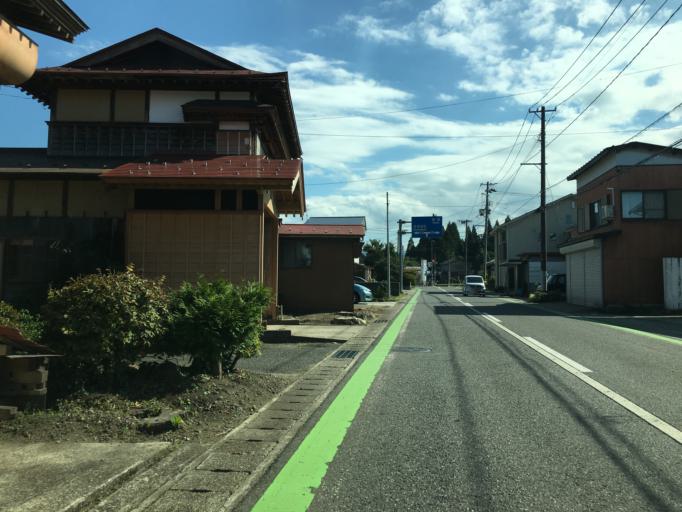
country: JP
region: Niigata
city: Suibara
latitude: 37.6670
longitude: 139.4704
